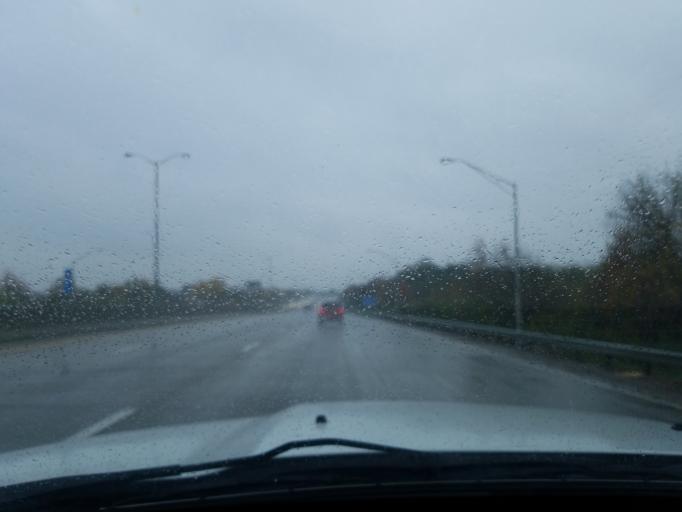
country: US
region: Kentucky
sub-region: Jefferson County
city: Shively
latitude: 38.2199
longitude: -85.8225
